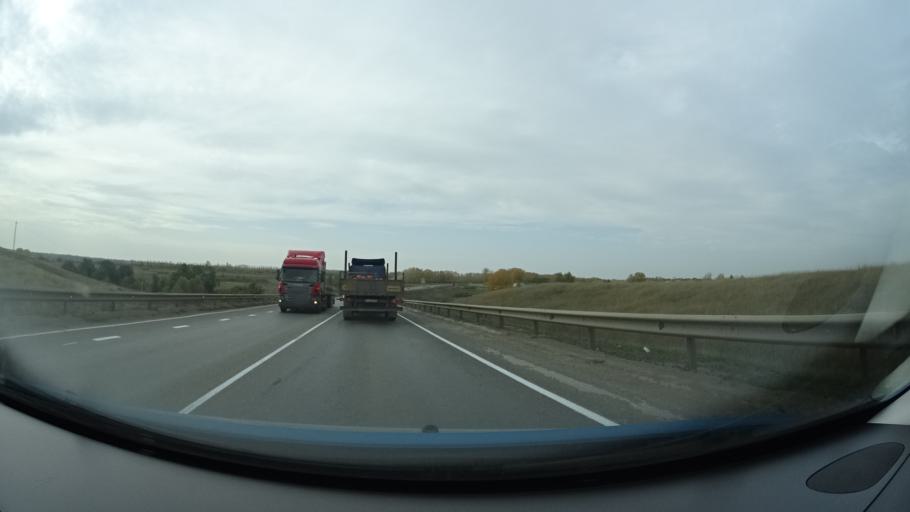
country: RU
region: Bashkortostan
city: Buzdyak
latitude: 54.6682
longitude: 54.7437
